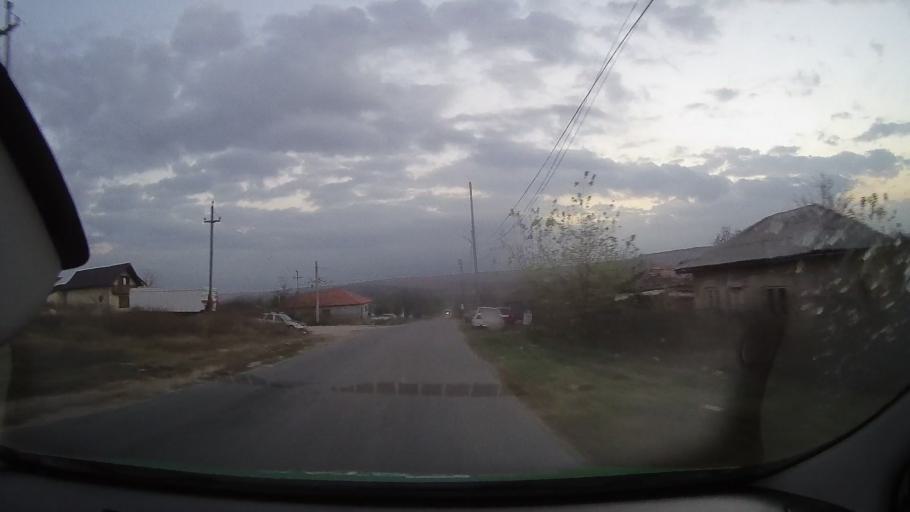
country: RO
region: Constanta
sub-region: Comuna Baneasa
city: Baneasa
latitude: 44.0764
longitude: 27.6967
